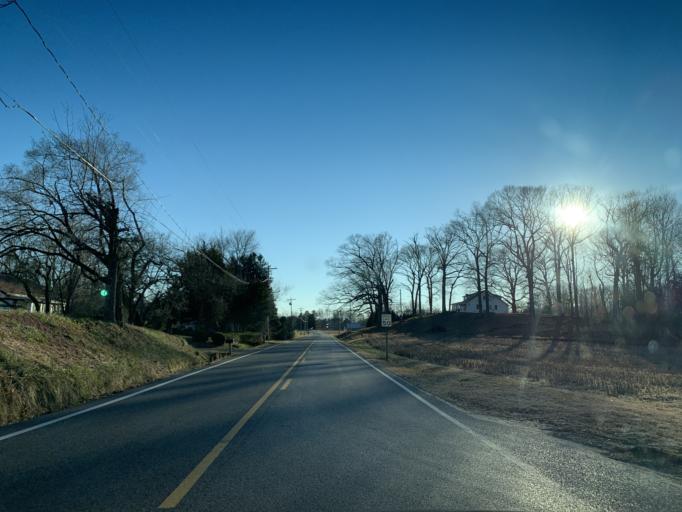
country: US
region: Maryland
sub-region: Saint Mary's County
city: Golden Beach
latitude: 38.4345
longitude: -76.6833
